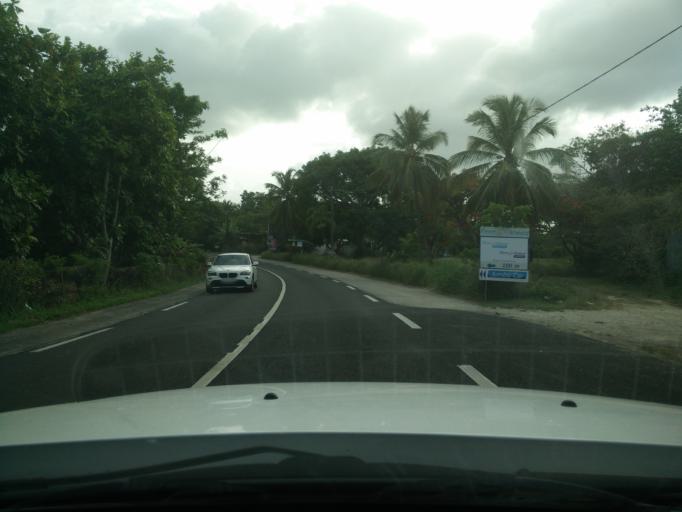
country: GP
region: Guadeloupe
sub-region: Guadeloupe
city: Sainte-Anne
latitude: 16.2538
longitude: -61.3322
